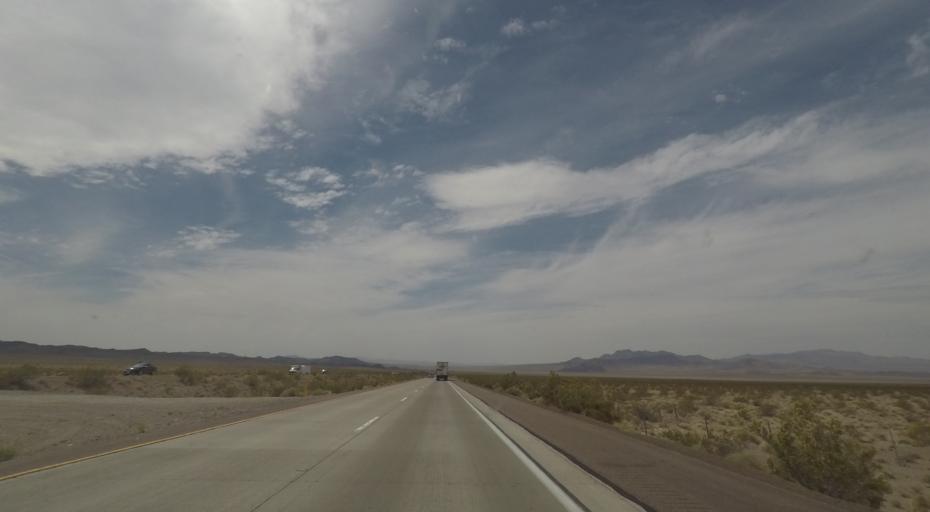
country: US
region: California
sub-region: San Bernardino County
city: Twentynine Palms
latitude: 34.7275
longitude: -116.0973
